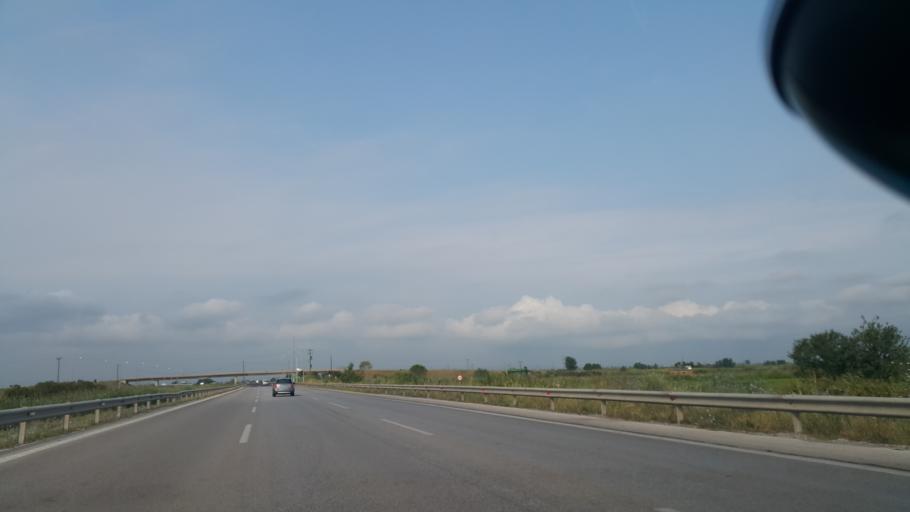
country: GR
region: Central Macedonia
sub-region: Nomos Imathias
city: Kleidi
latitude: 40.5785
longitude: 22.6338
